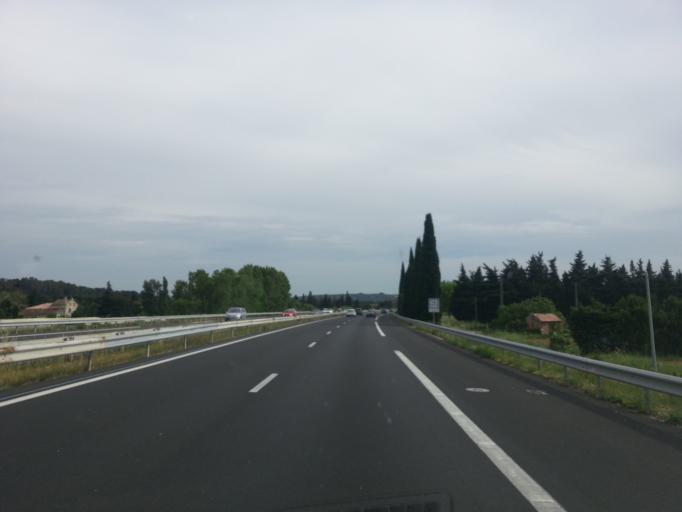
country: FR
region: Provence-Alpes-Cote d'Azur
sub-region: Departement du Vaucluse
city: Caderousse
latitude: 44.1083
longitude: 4.7891
